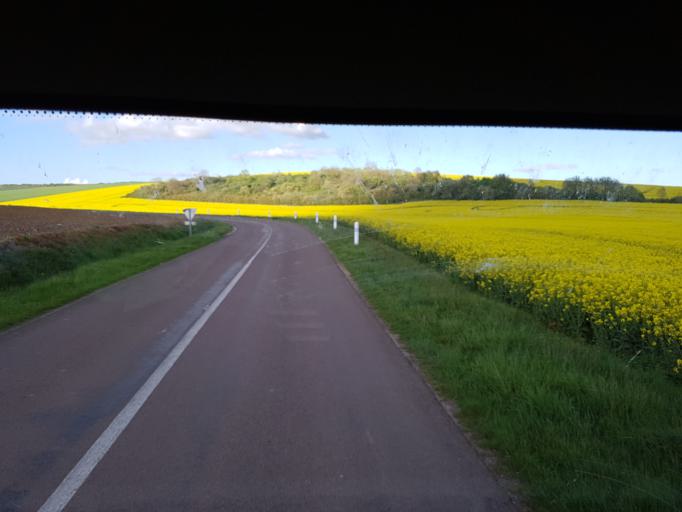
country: FR
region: Champagne-Ardenne
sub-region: Departement de l'Aube
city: Aix-en-Othe
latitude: 48.2338
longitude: 3.6326
